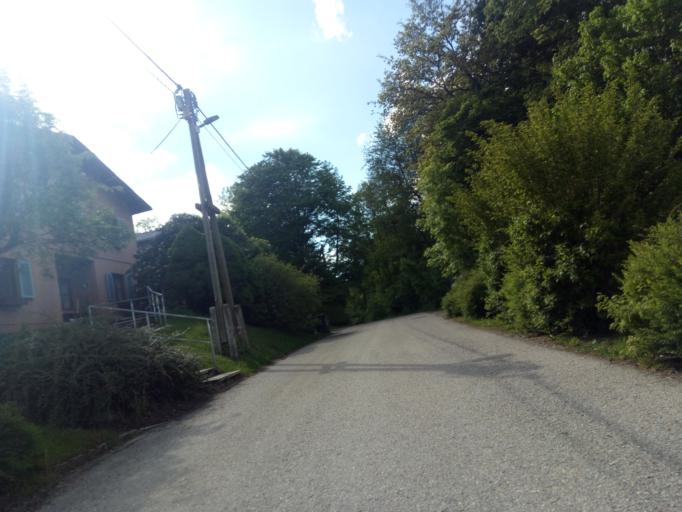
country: AT
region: Lower Austria
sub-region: Politischer Bezirk Modling
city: Breitenfurt bei Wien
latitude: 48.1338
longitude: 16.1447
